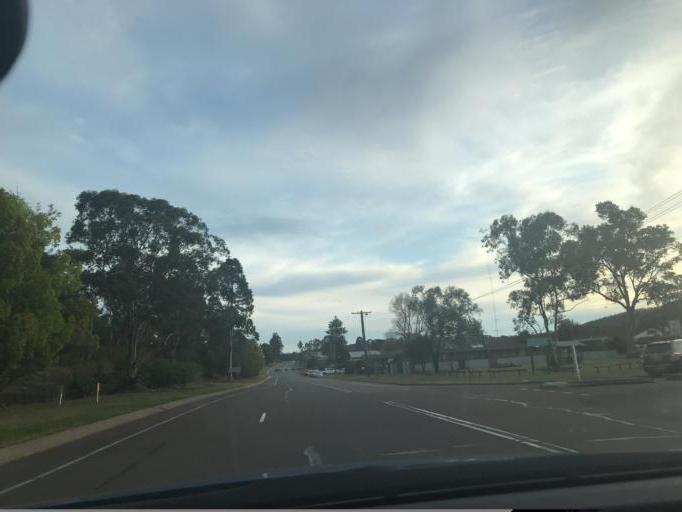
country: AU
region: New South Wales
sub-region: Cessnock
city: Cessnock
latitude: -32.8596
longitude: 151.3207
